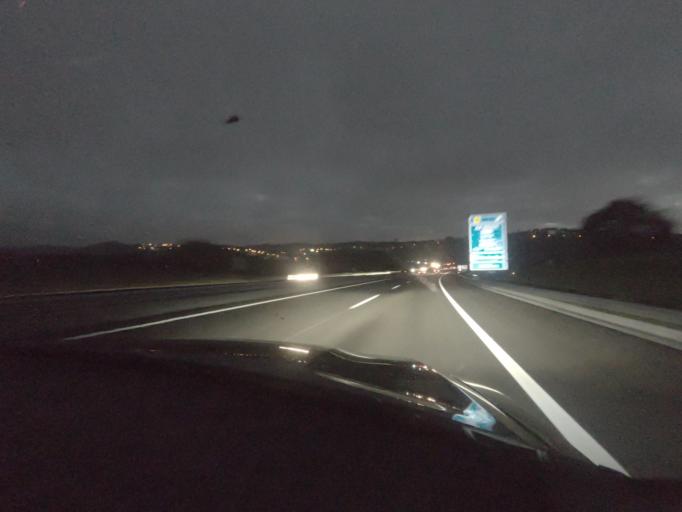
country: PT
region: Leiria
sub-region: Leiria
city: Caranguejeira
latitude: 39.7600
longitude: -8.7464
